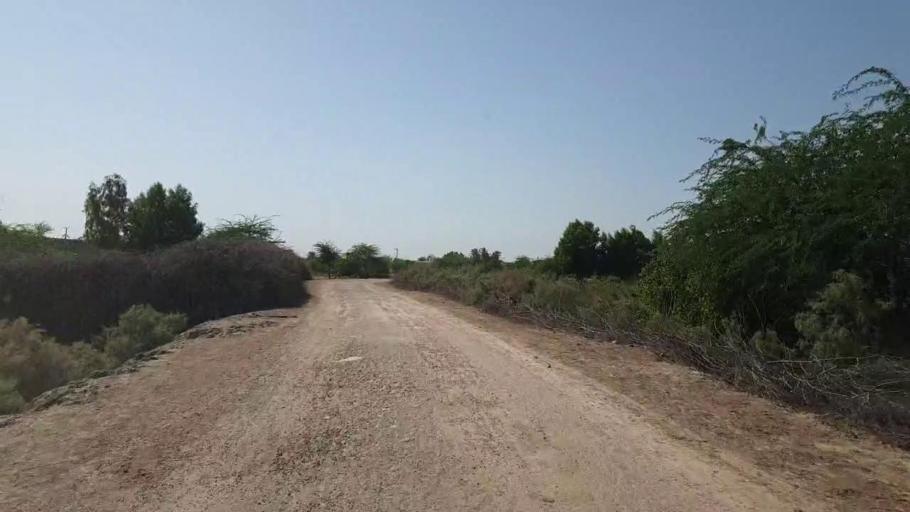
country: PK
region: Sindh
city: Tando Bago
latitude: 24.7051
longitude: 69.0399
